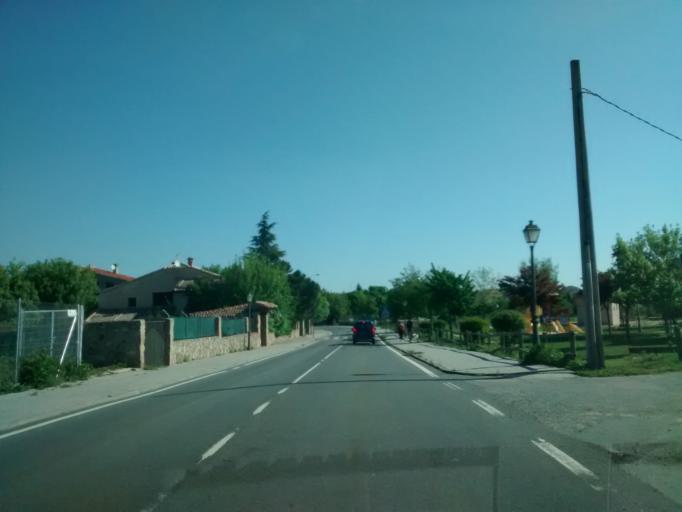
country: ES
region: Castille and Leon
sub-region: Provincia de Segovia
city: Torrecaballeros
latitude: 40.9925
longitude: -4.0226
